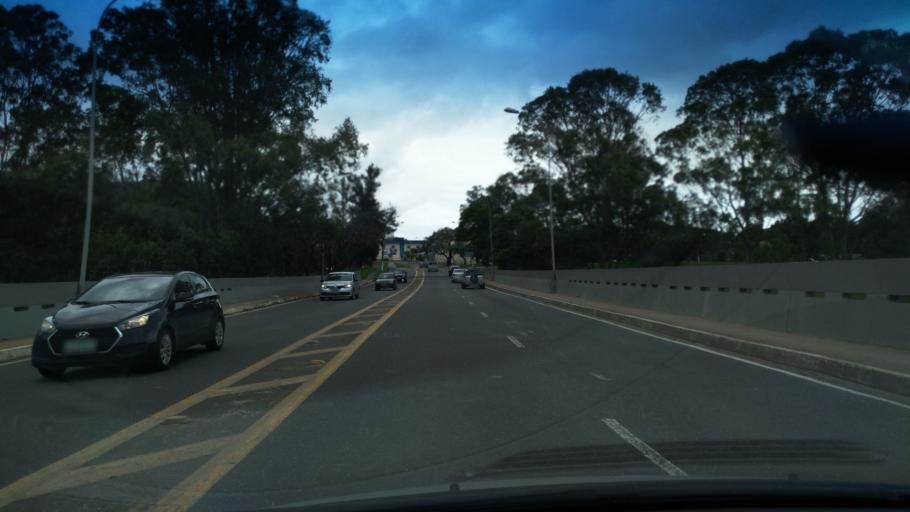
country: BR
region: Sao Paulo
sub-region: Valinhos
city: Valinhos
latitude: -22.9641
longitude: -46.9943
